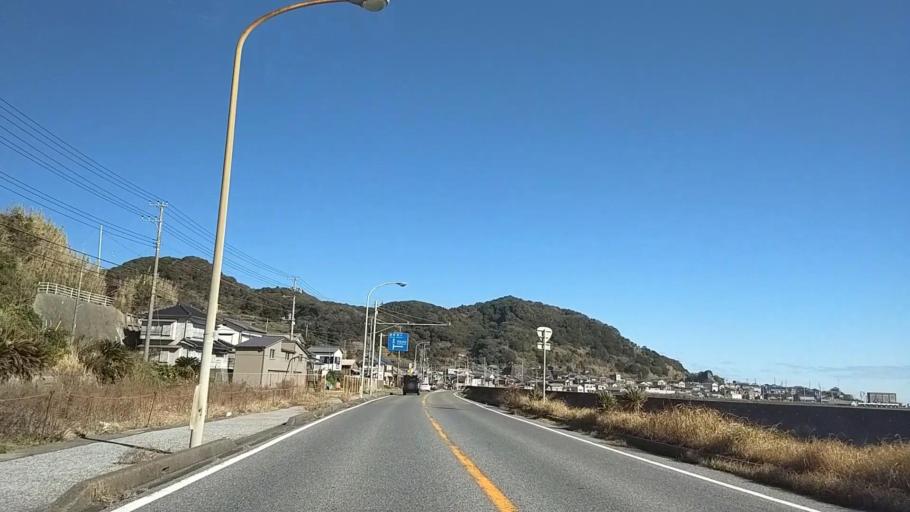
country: JP
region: Chiba
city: Kawaguchi
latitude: 35.0344
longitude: 140.0078
